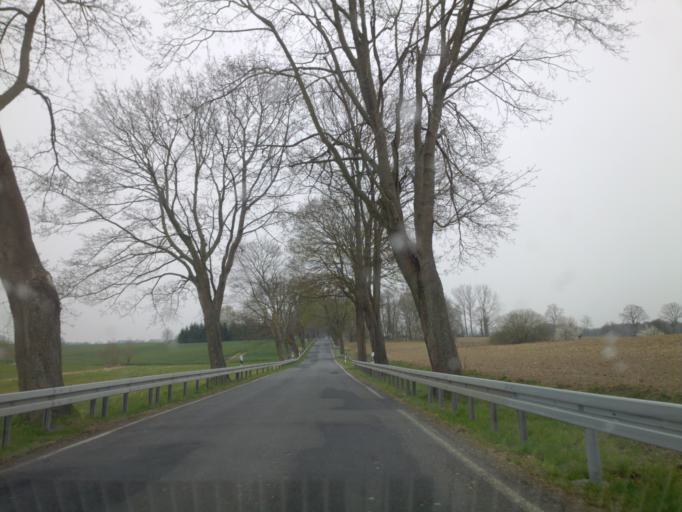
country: DE
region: Mecklenburg-Vorpommern
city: Bad Sulze
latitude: 54.1566
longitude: 12.7087
